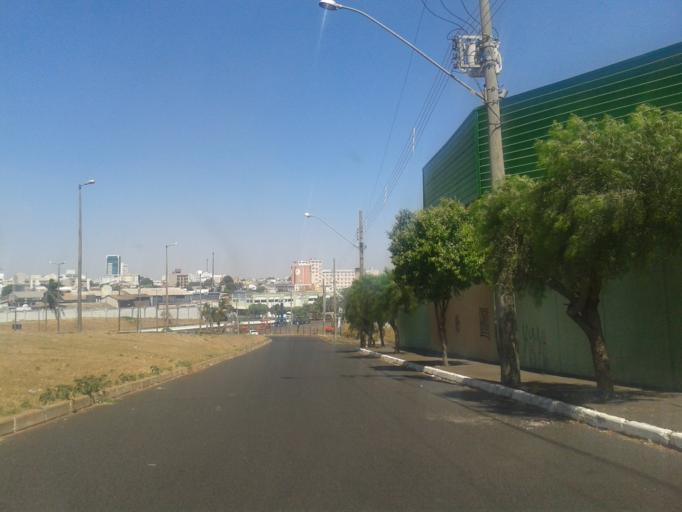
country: BR
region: Minas Gerais
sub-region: Uberlandia
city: Uberlandia
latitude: -18.8948
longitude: -48.2726
